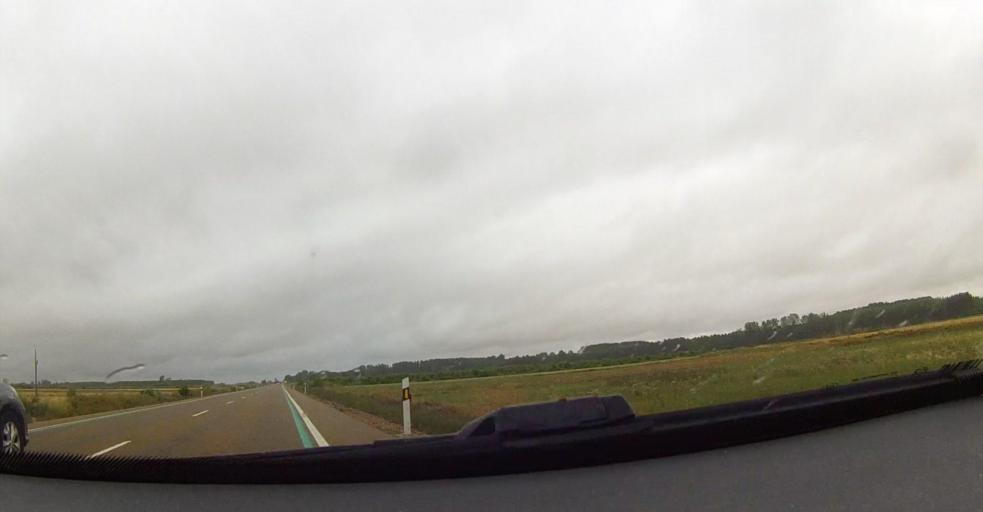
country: ES
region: Castille and Leon
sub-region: Provincia de Palencia
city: Nogal de las Huertas
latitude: 42.3595
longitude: -4.6321
